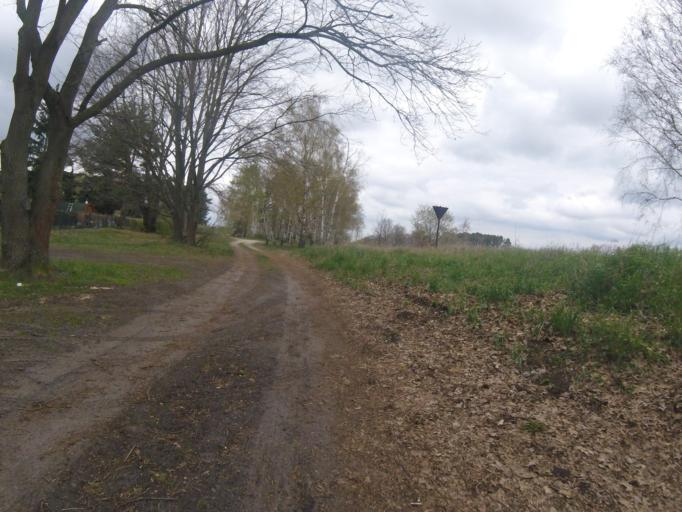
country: DE
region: Brandenburg
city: Mittenwalde
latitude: 52.2507
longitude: 13.5667
